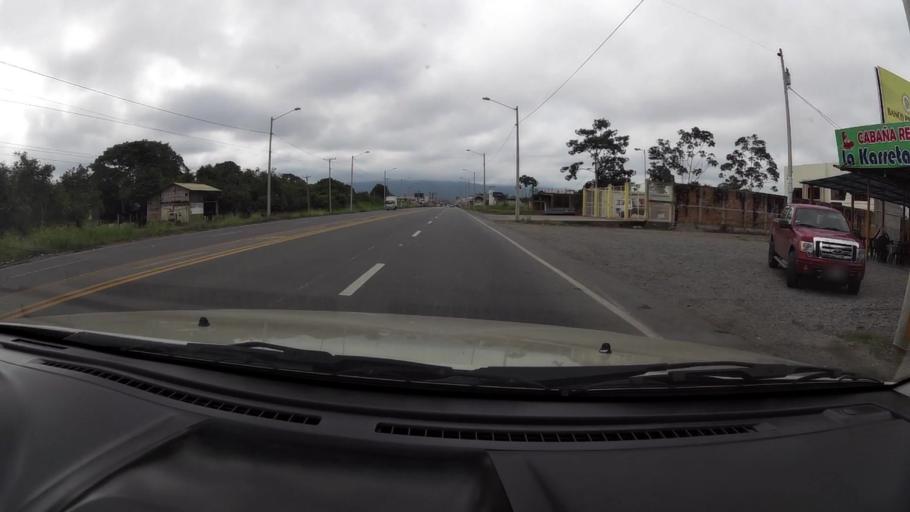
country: EC
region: Guayas
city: Naranjal
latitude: -2.6615
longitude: -79.6158
